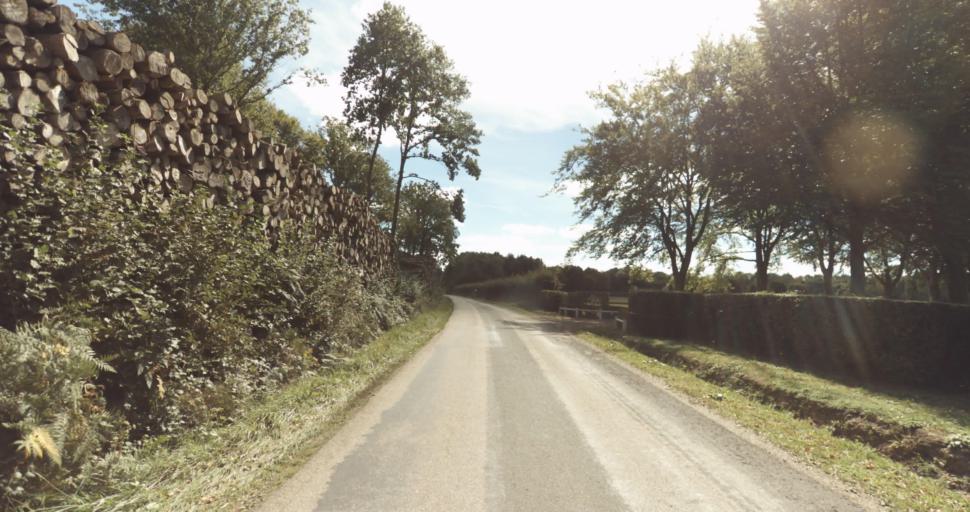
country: FR
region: Lower Normandy
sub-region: Departement de l'Orne
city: Vimoutiers
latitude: 48.9218
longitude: 0.2485
